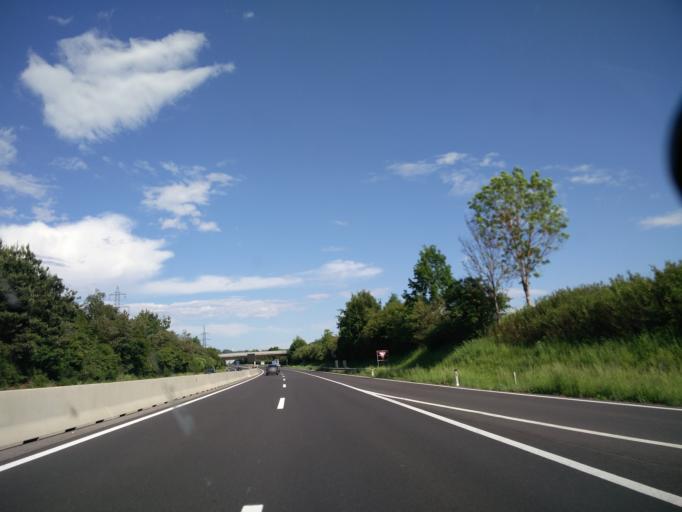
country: AT
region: Carinthia
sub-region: Politischer Bezirk Volkermarkt
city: Voelkermarkt
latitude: 46.6841
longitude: 14.6623
